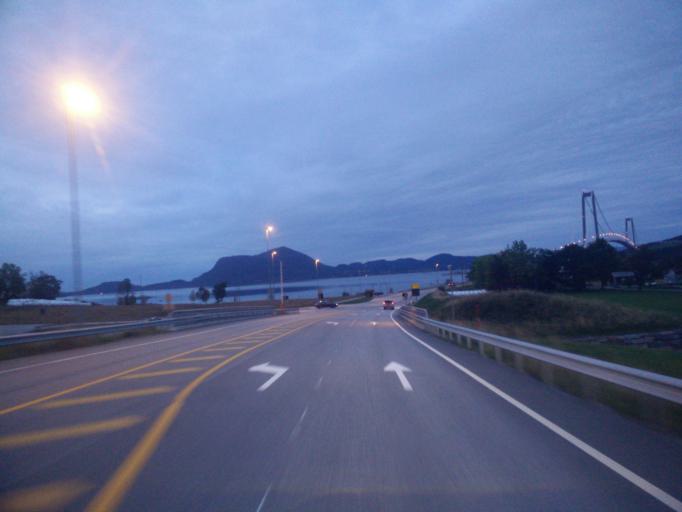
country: NO
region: More og Romsdal
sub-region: Gjemnes
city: Batnfjordsora
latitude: 62.9627
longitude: 7.7684
